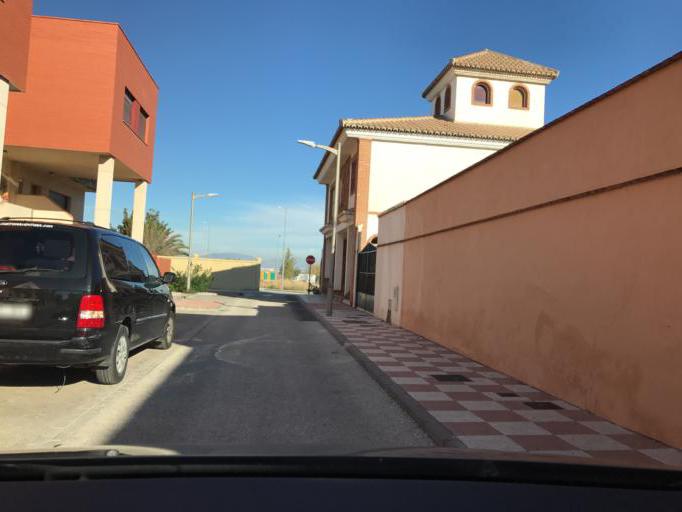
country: ES
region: Andalusia
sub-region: Provincia de Granada
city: Churriana de la Vega
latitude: 37.1481
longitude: -3.6535
